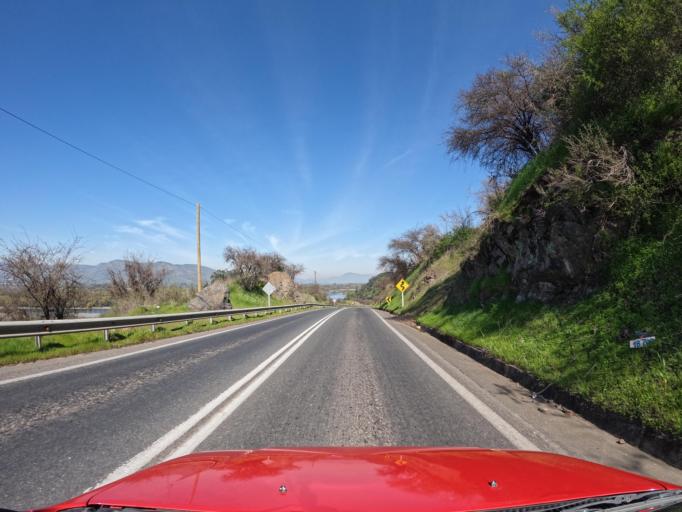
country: CL
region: Maule
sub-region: Provincia de Curico
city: Rauco
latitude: -34.9759
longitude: -71.3836
